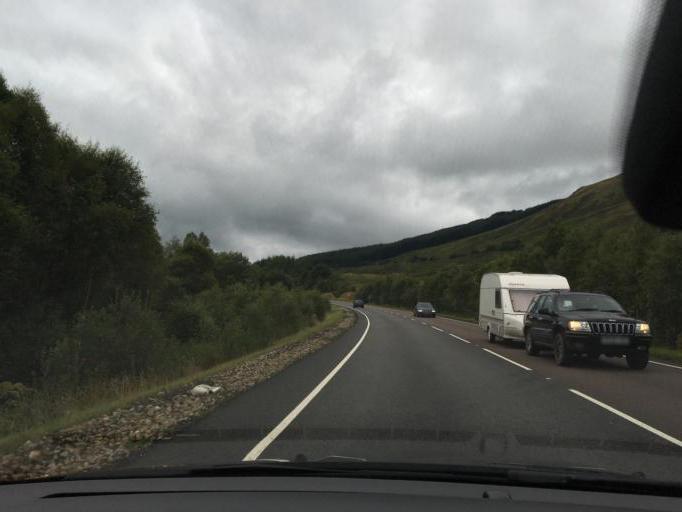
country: GB
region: Scotland
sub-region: Argyll and Bute
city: Garelochhead
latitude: 56.4228
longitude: -4.6780
